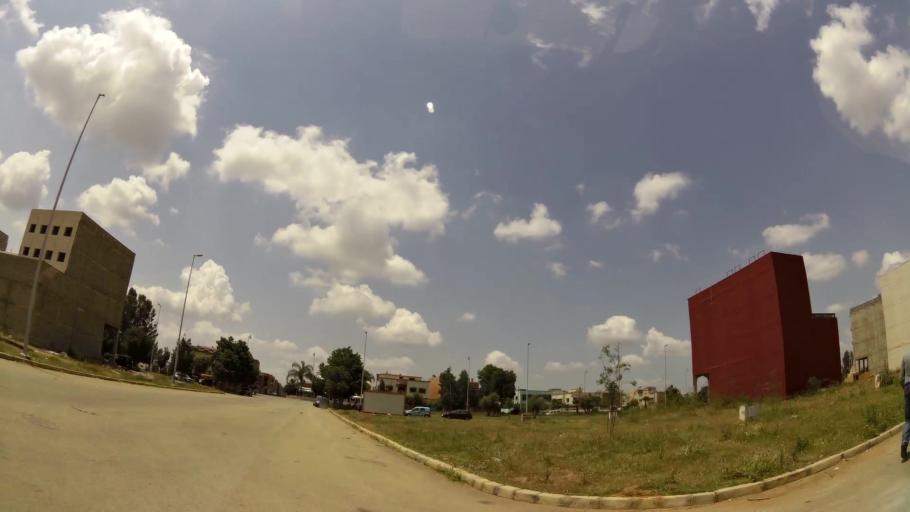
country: MA
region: Rabat-Sale-Zemmour-Zaer
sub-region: Khemisset
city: Tiflet
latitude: 34.0088
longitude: -6.5245
